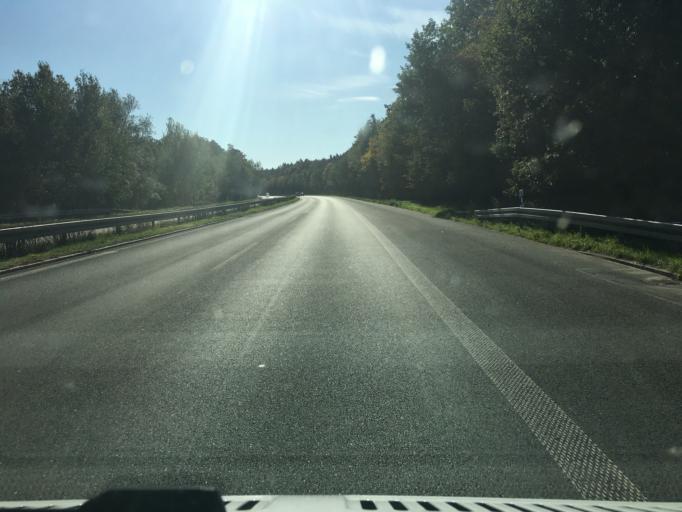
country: DE
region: Saxony
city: Dennheritz
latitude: 50.8000
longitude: 12.4549
